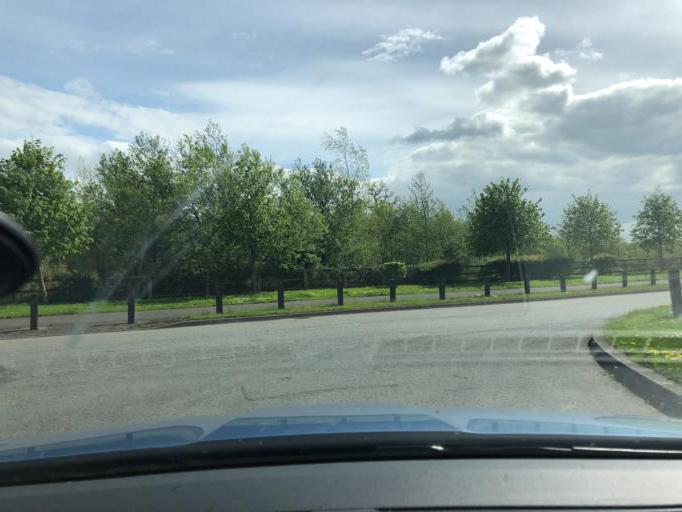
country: IE
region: Leinster
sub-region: Kildare
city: Johnstown
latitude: 53.2441
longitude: -6.6100
